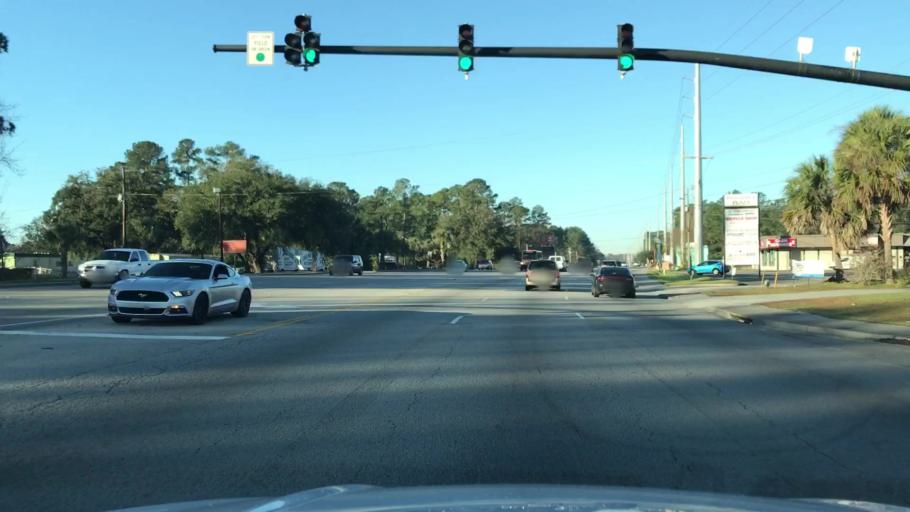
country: US
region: South Carolina
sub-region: Berkeley County
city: Hanahan
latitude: 32.9254
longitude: -80.0828
